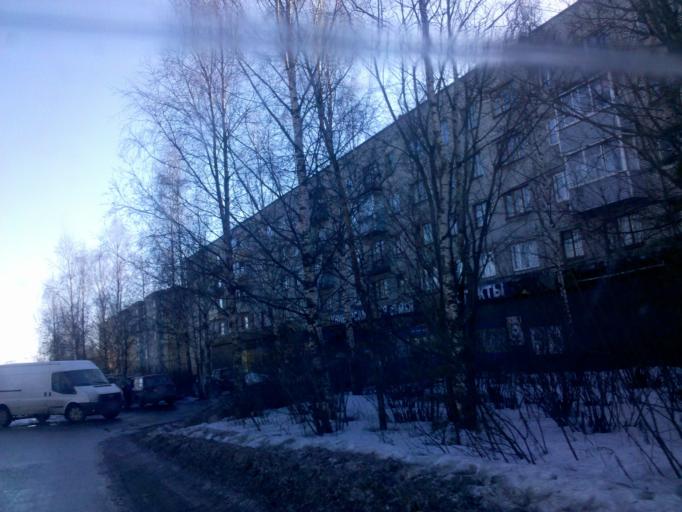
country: RU
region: Republic of Karelia
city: Medvezh'yegorsk
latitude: 62.9146
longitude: 34.4751
